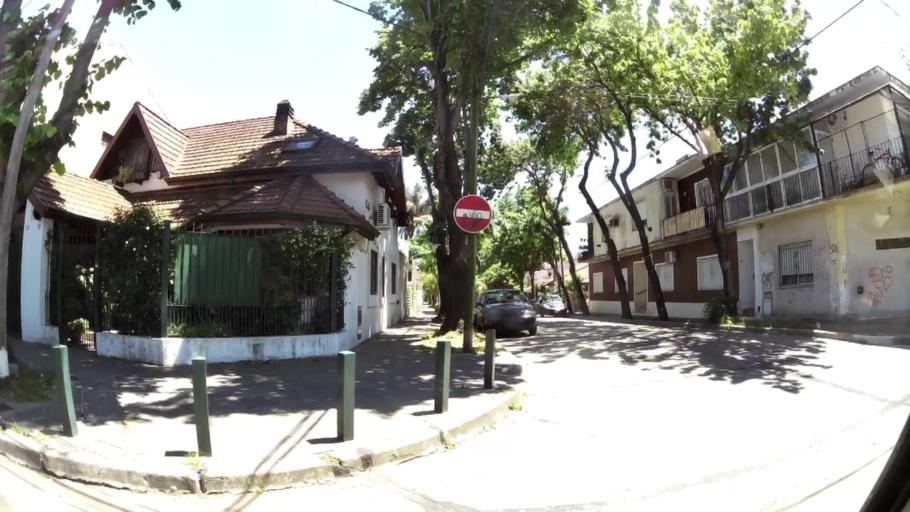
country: AR
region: Buenos Aires
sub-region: Partido de Vicente Lopez
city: Olivos
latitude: -34.5026
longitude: -58.4994
